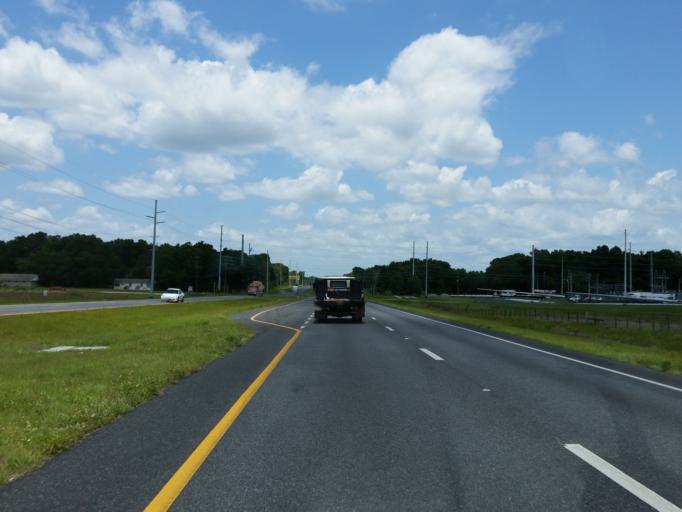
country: US
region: Florida
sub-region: Sumter County
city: The Villages
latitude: 28.9681
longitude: -82.0411
